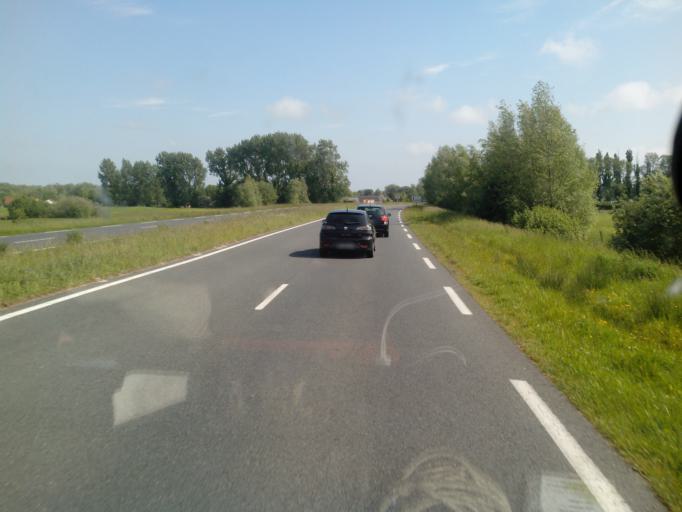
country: FR
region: Picardie
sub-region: Departement de la Somme
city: Rue
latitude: 50.2806
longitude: 1.6584
